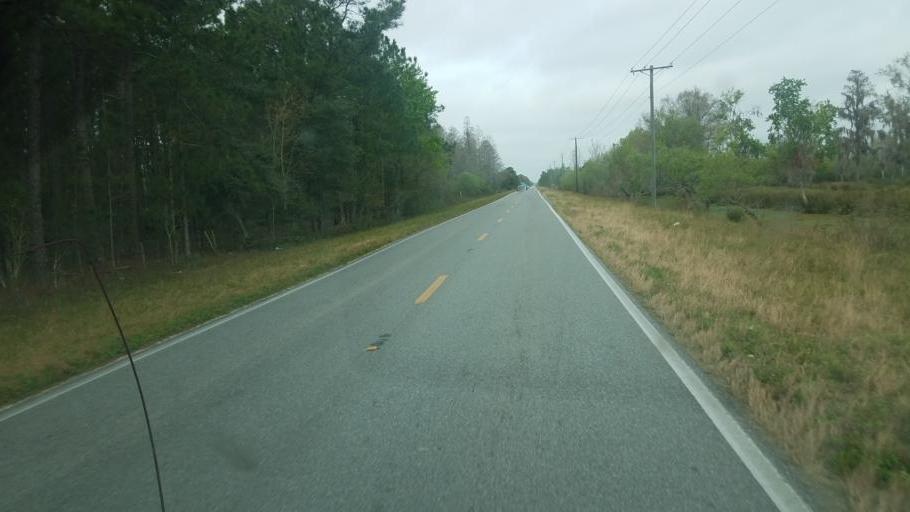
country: US
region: Florida
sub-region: Polk County
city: Polk City
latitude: 28.2590
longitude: -81.9062
